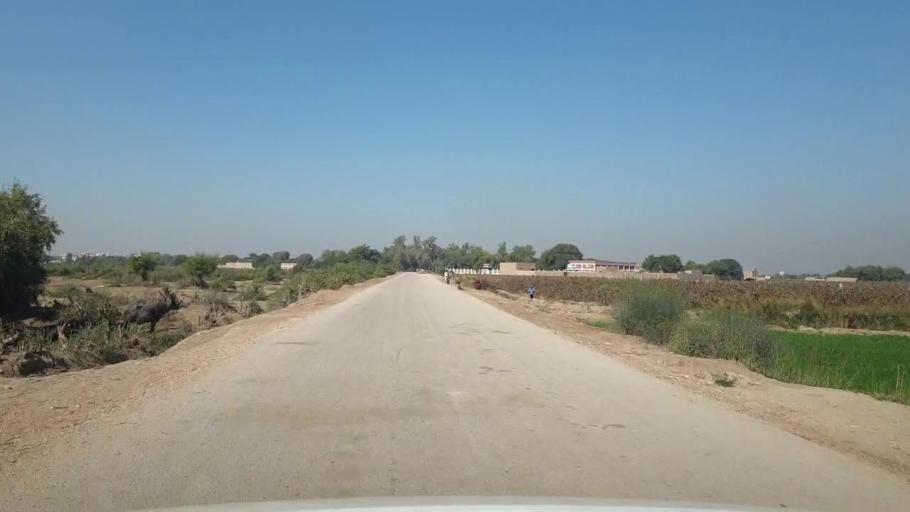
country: PK
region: Sindh
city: Bhan
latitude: 26.6470
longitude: 67.7161
